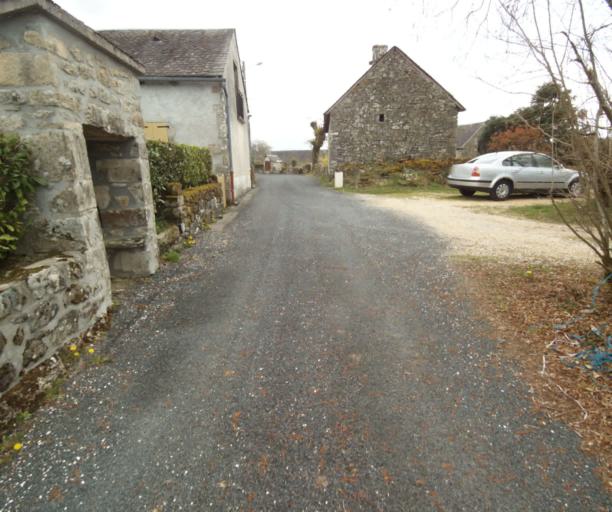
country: FR
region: Limousin
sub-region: Departement de la Correze
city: Argentat
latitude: 45.2131
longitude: 1.9181
